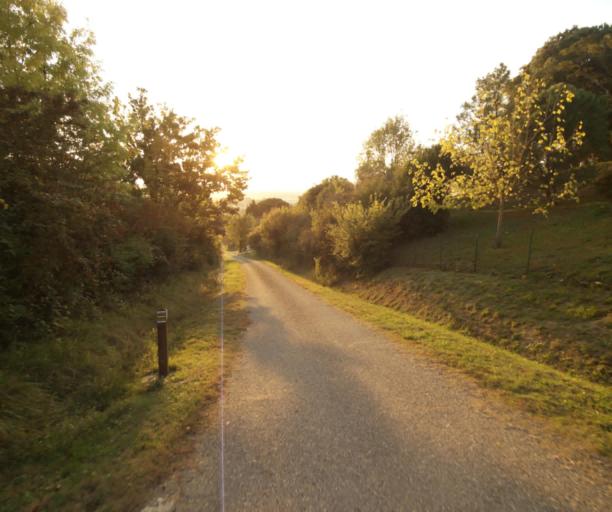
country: FR
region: Midi-Pyrenees
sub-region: Departement du Tarn-et-Garonne
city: Grisolles
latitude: 43.8317
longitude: 1.3072
